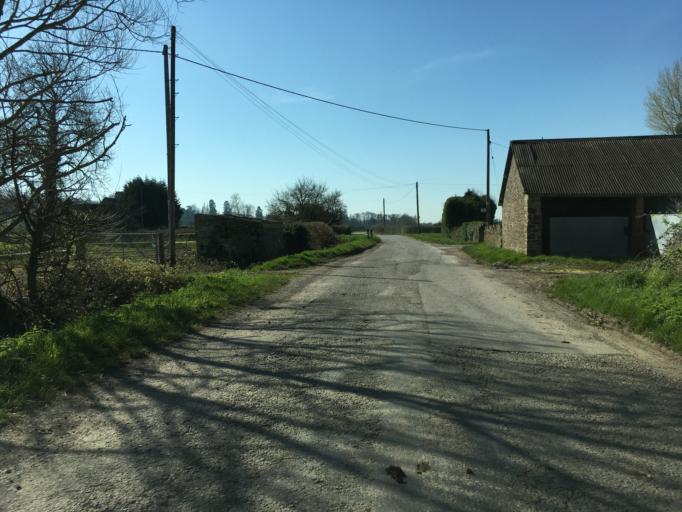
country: GB
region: England
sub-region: South Gloucestershire
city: Hill
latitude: 51.6627
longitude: -2.5069
